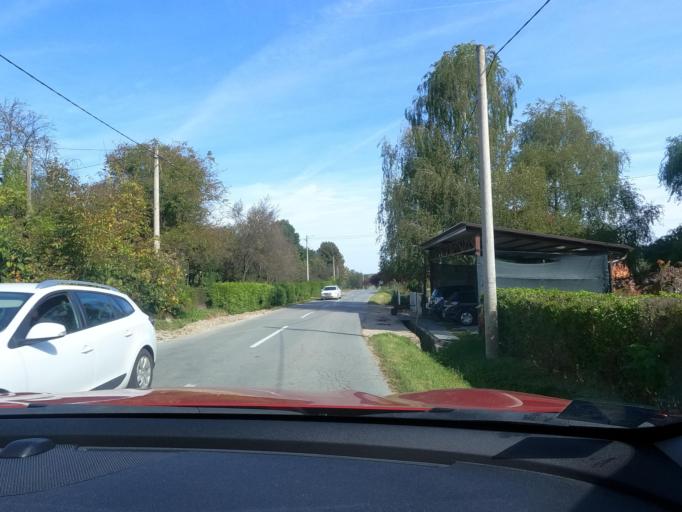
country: HR
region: Sisacko-Moslavacka
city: Petrinja
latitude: 45.4041
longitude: 16.2899
